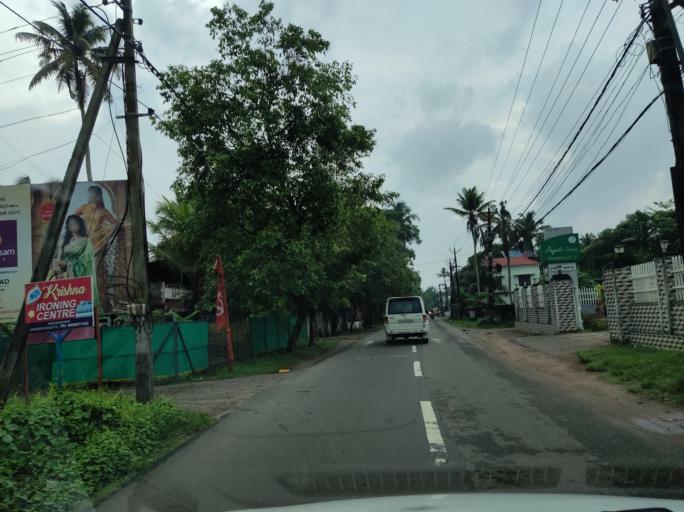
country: IN
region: Kerala
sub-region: Alappuzha
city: Kayankulam
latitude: 9.2584
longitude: 76.4287
